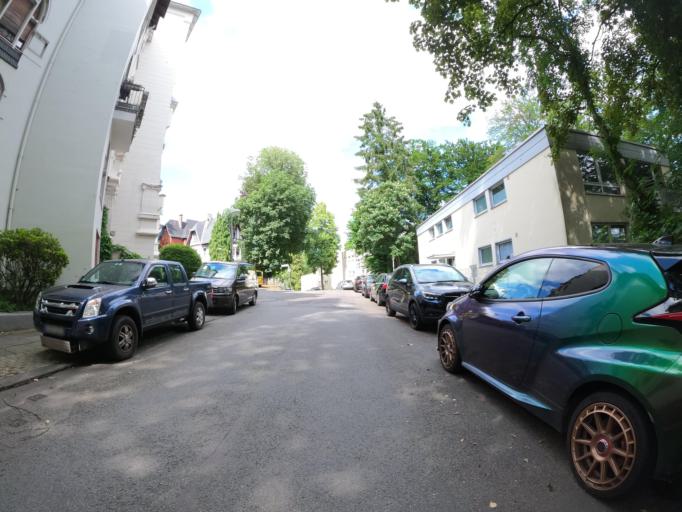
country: DE
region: North Rhine-Westphalia
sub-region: Regierungsbezirk Dusseldorf
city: Wuppertal
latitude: 51.2520
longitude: 7.1262
